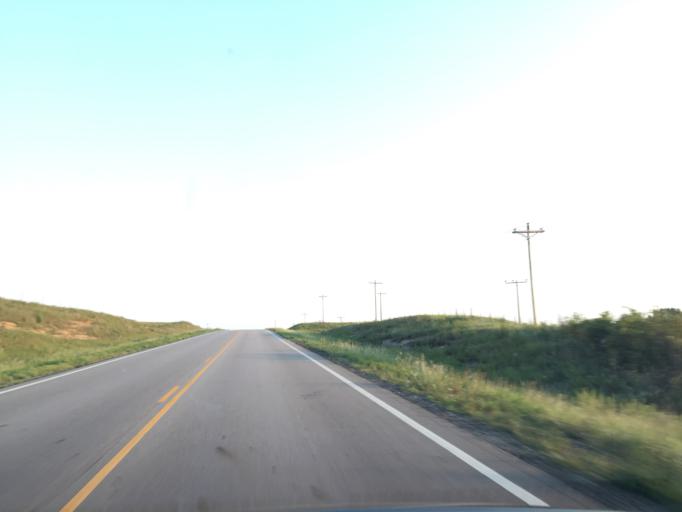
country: US
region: Kansas
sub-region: Ellsworth County
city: Ellsworth
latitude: 38.5942
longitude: -98.2016
